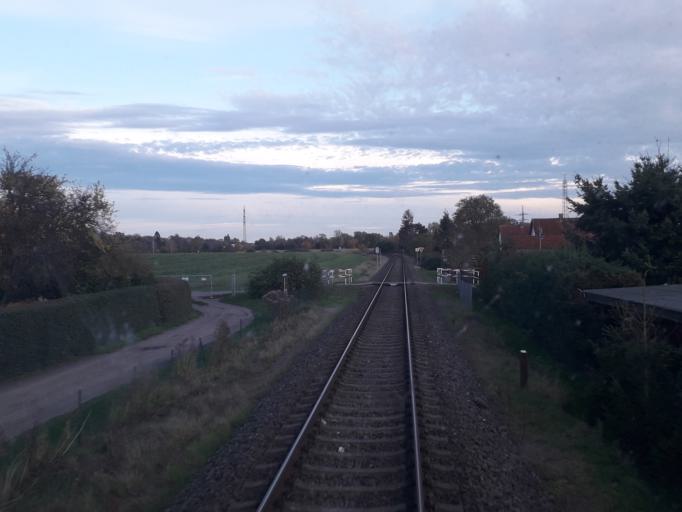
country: DE
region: Brandenburg
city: Neuruppin
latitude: 52.9246
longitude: 12.7823
